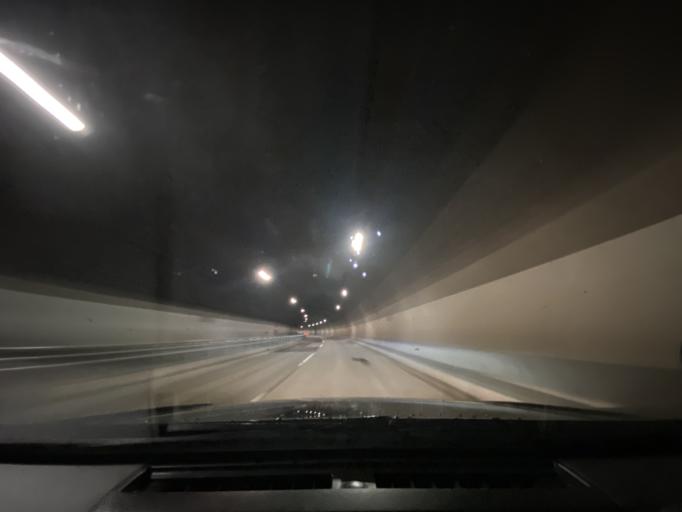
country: JP
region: Hokkaido
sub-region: Asahikawa-shi
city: Asahikawa
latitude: 43.7707
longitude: 142.3036
